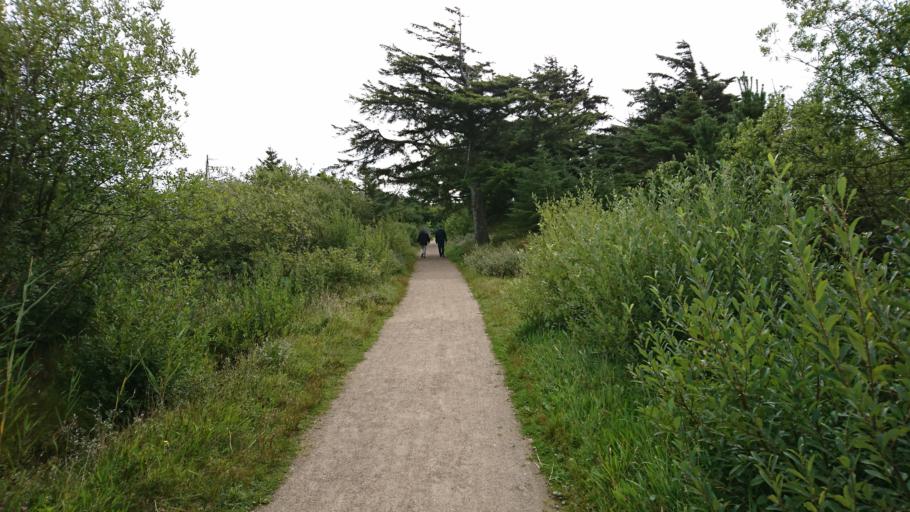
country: DK
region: South Denmark
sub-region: Fano Kommune
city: Nordby
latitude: 55.3889
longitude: 8.4072
